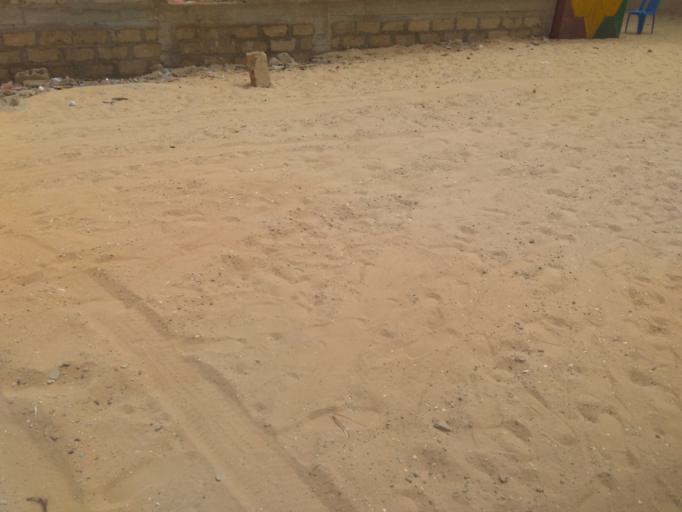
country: SN
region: Dakar
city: Pikine
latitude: 14.7987
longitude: -17.3394
